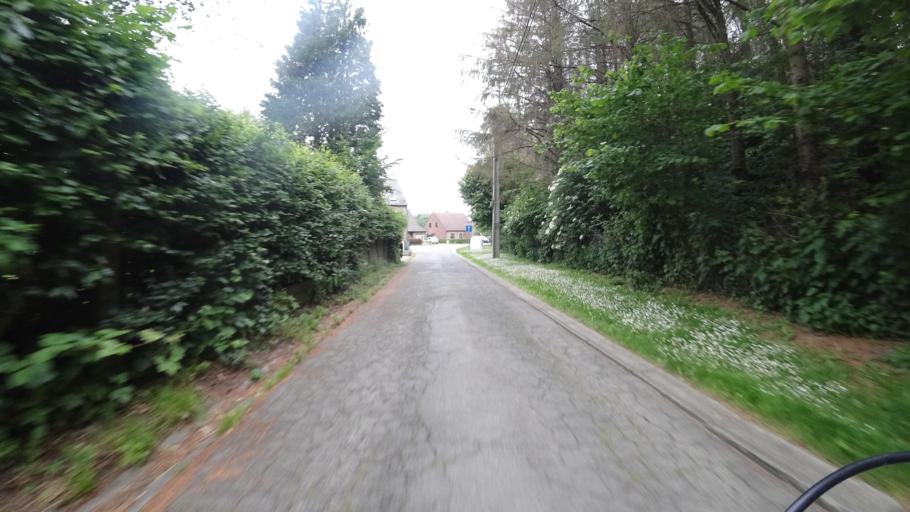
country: BE
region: Wallonia
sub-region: Province du Brabant Wallon
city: Perwez
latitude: 50.5704
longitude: 4.7710
